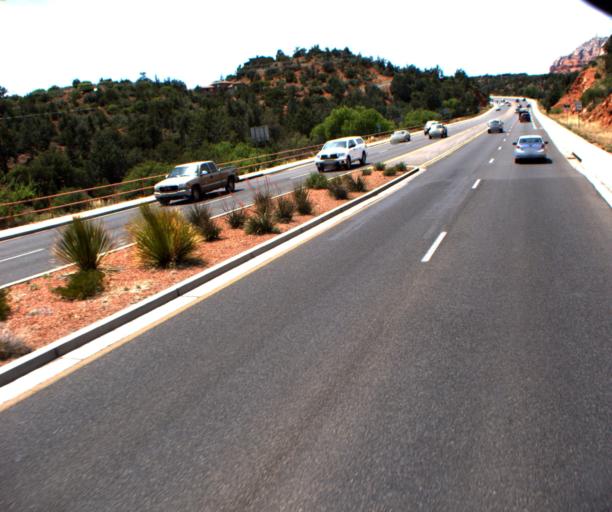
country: US
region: Arizona
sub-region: Coconino County
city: Sedona
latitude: 34.8663
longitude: -111.7656
